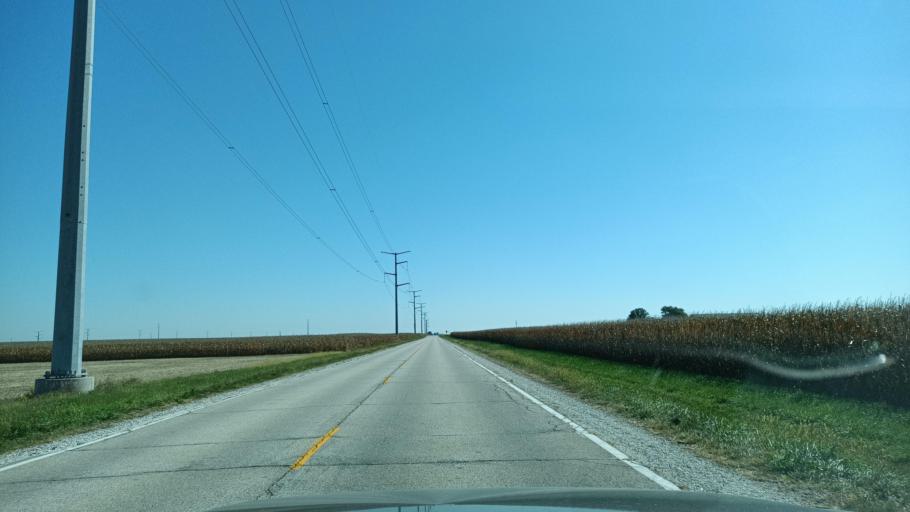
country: US
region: Illinois
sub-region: Peoria County
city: Elmwood
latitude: 40.9023
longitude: -89.9915
